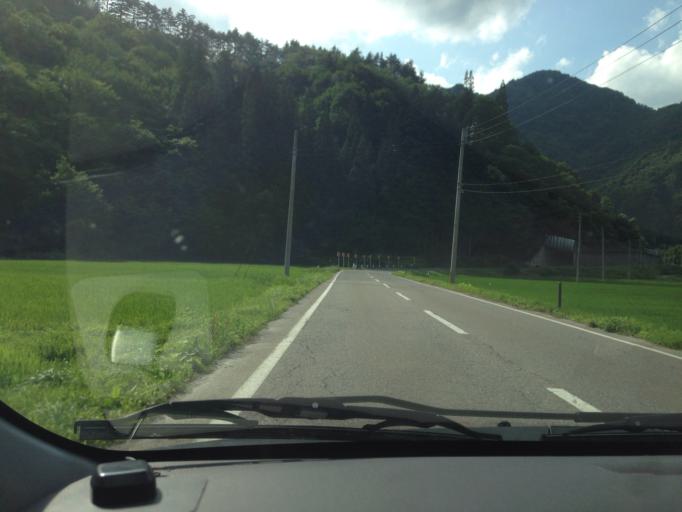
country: JP
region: Fukushima
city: Kitakata
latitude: 37.3780
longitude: 139.5493
